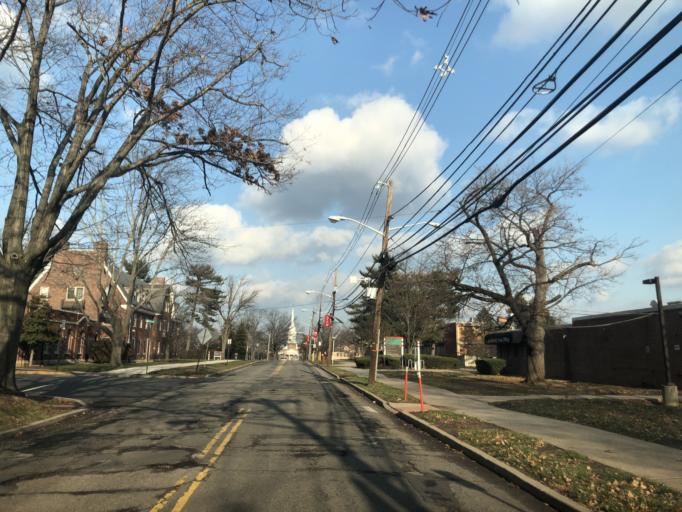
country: US
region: New Jersey
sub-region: Middlesex County
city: New Brunswick
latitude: 40.4834
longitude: -74.4389
